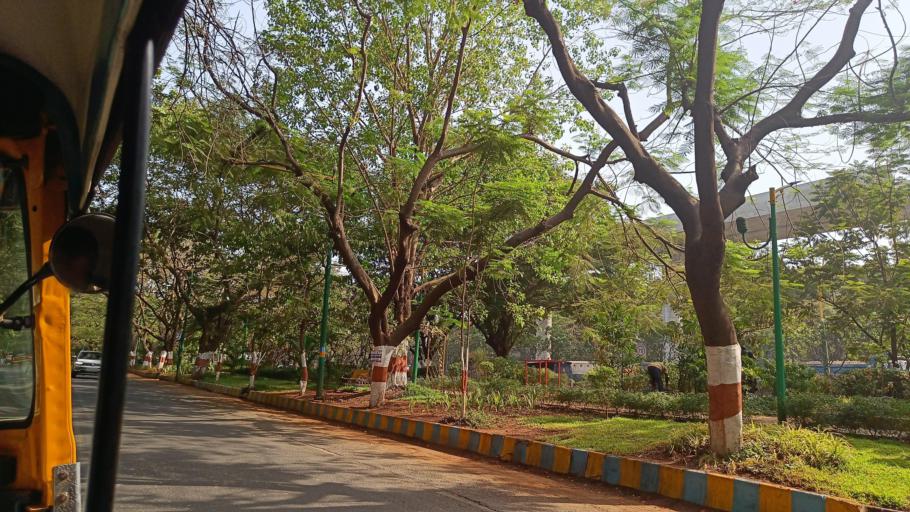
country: IN
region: Maharashtra
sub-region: Thane
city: Thane
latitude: 19.1926
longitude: 72.9633
